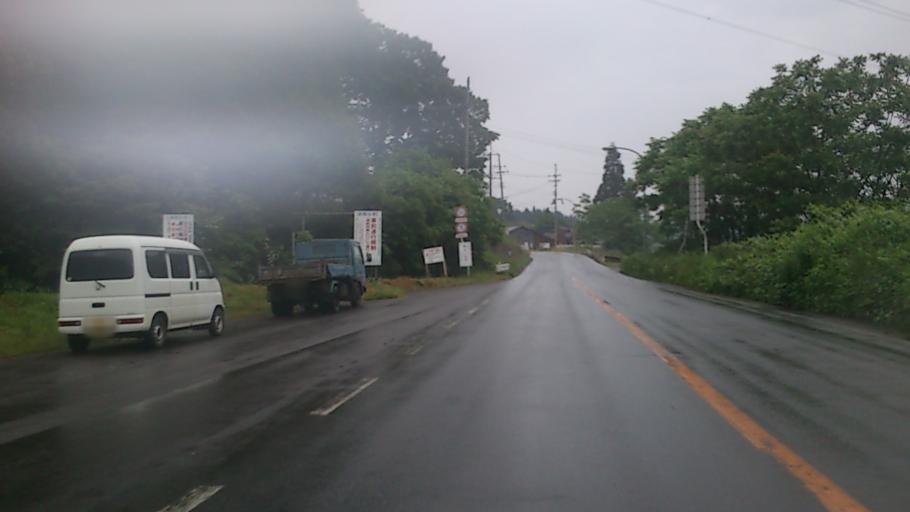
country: JP
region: Akita
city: Takanosu
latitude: 40.2401
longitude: 140.2444
